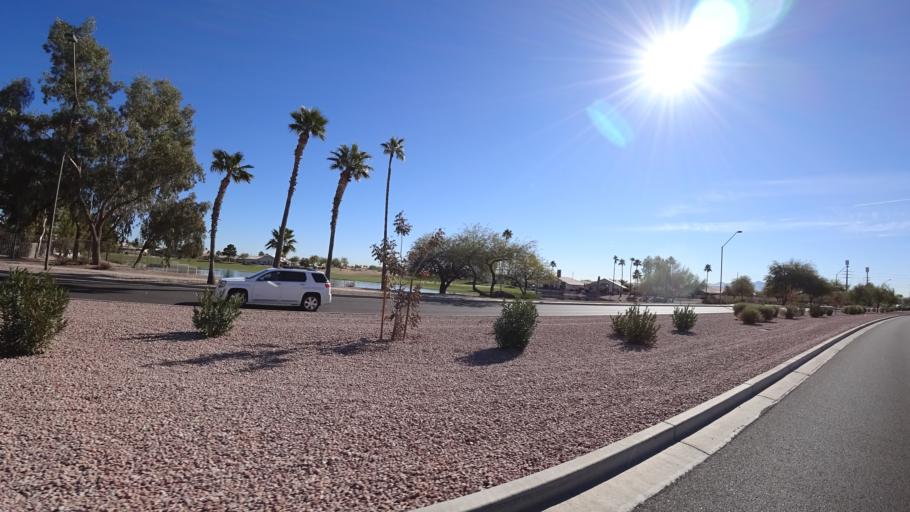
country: US
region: Arizona
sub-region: Maricopa County
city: Litchfield Park
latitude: 33.4812
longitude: -112.3927
